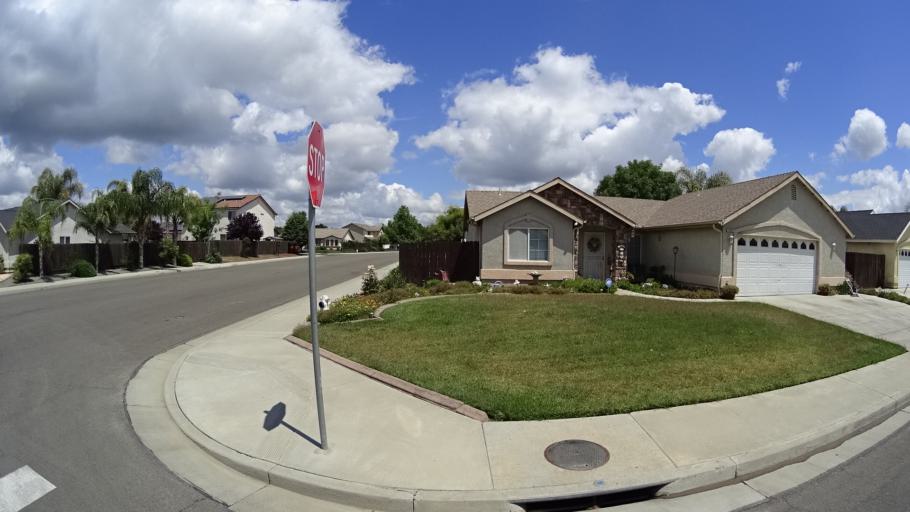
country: US
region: California
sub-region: Kings County
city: Lucerne
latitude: 36.3532
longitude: -119.6622
